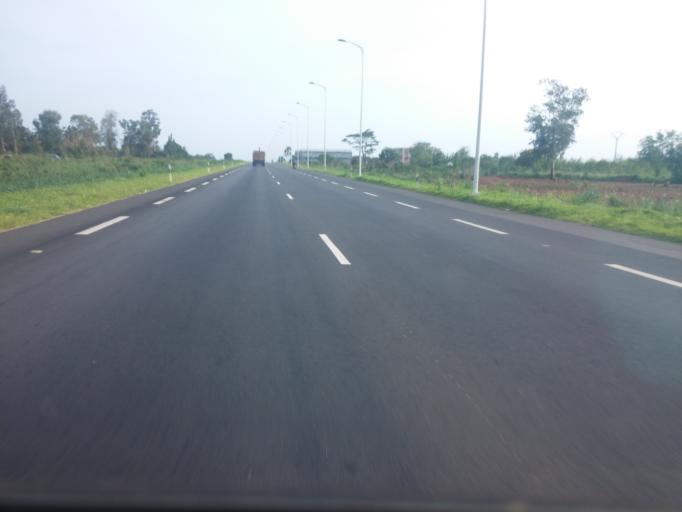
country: TG
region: Maritime
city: Tsevie
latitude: 6.3602
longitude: 1.2096
